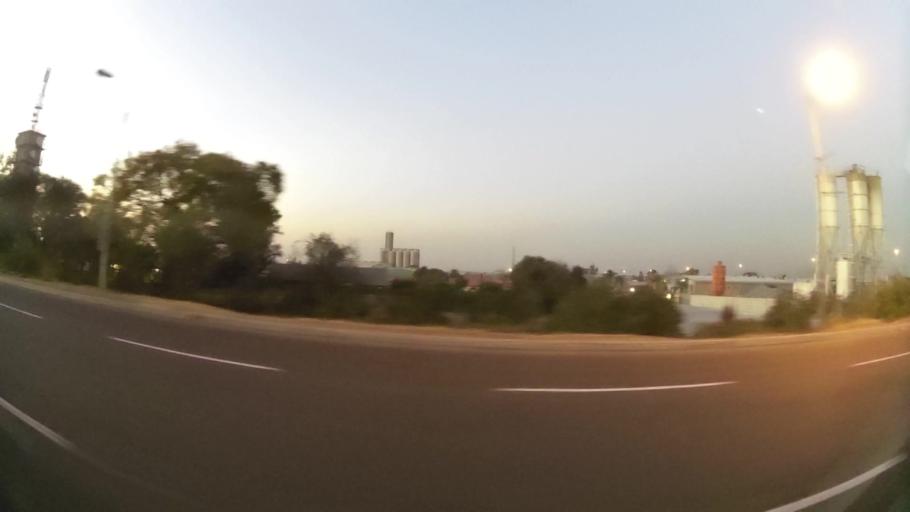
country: ZA
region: North-West
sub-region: Bojanala Platinum District Municipality
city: Rustenburg
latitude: -25.6805
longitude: 27.2543
